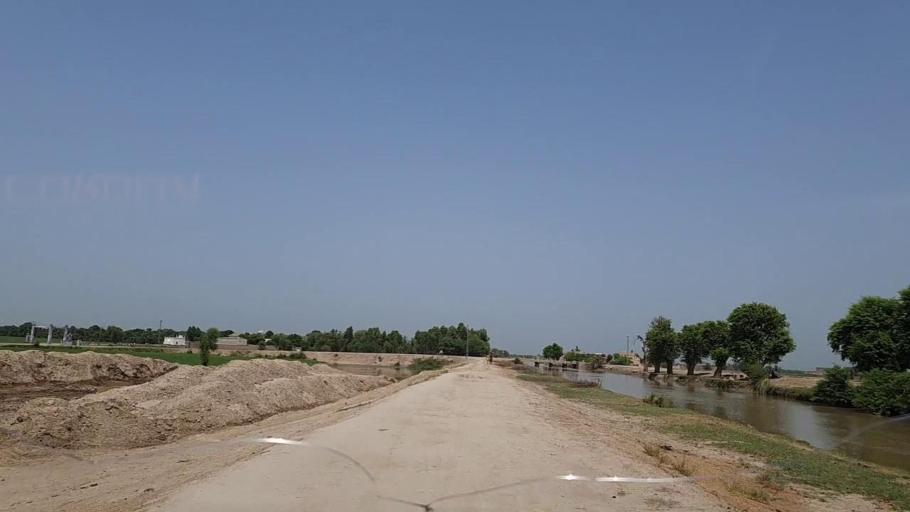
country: PK
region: Sindh
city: Tharu Shah
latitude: 26.9844
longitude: 68.0770
